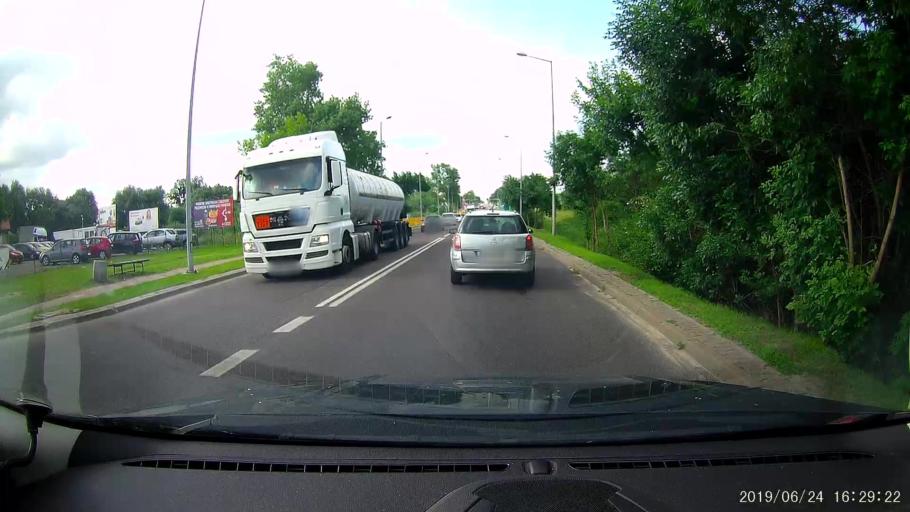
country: PL
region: Lublin Voivodeship
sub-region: Powiat tomaszowski
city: Tomaszow Lubelski
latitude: 50.4587
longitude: 23.4209
